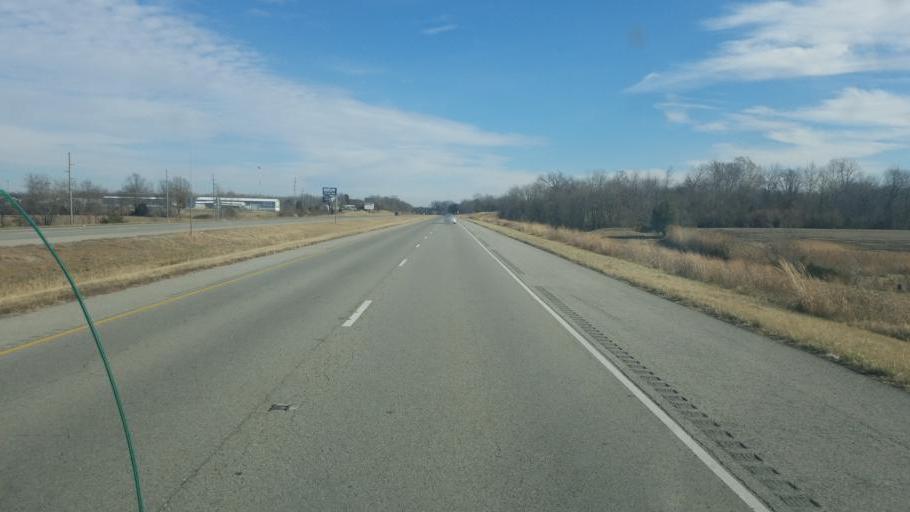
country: US
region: Illinois
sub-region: Williamson County
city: Marion
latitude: 37.7295
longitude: -88.8355
